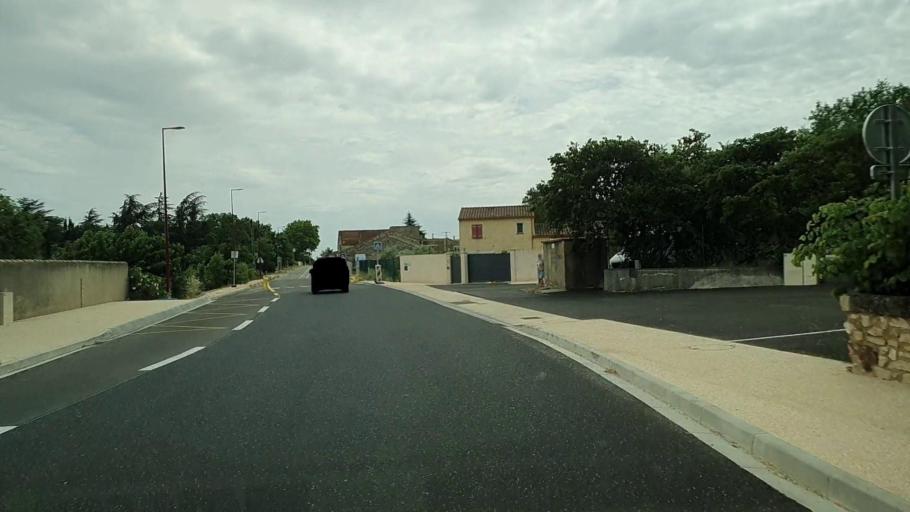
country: FR
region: Languedoc-Roussillon
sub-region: Departement du Gard
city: Connaux
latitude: 44.0397
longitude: 4.5813
